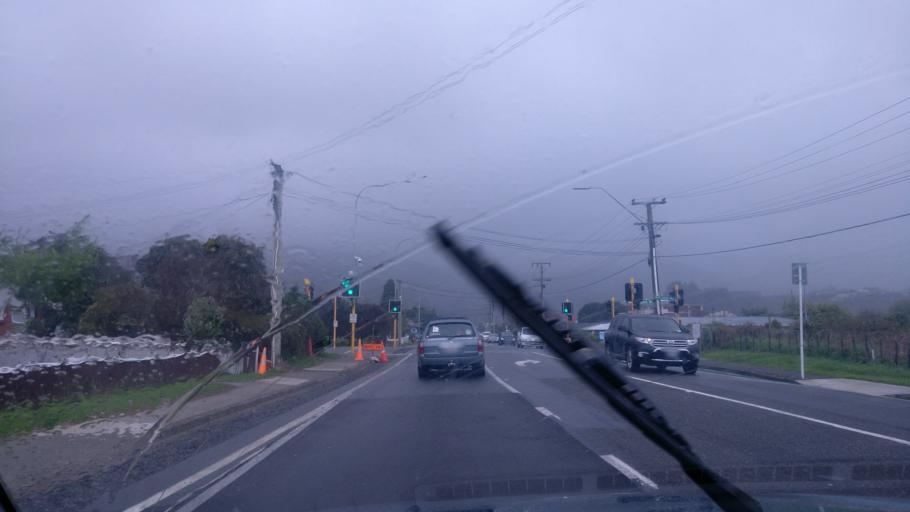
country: NZ
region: Wellington
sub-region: Kapiti Coast District
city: Paraparaumu
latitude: -40.9112
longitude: 175.0025
